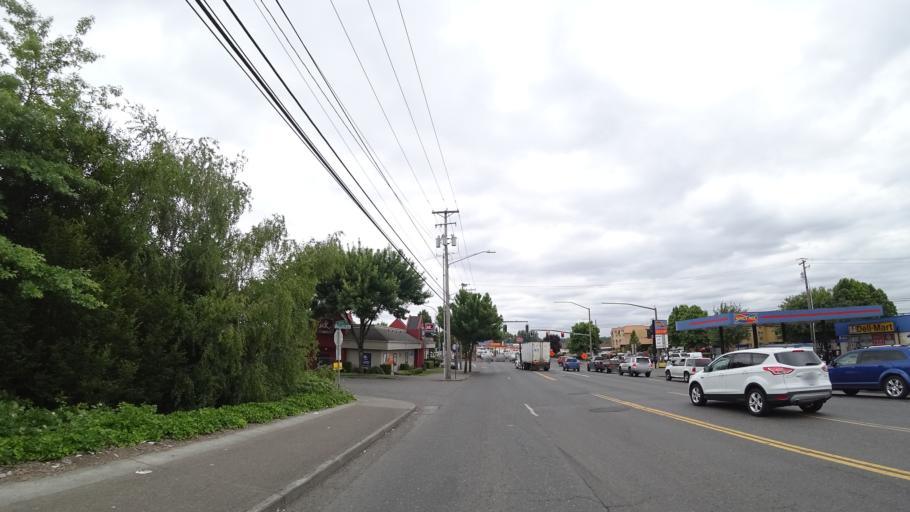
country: US
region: Washington
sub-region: Clark County
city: Vancouver
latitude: 45.5805
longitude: -122.6615
